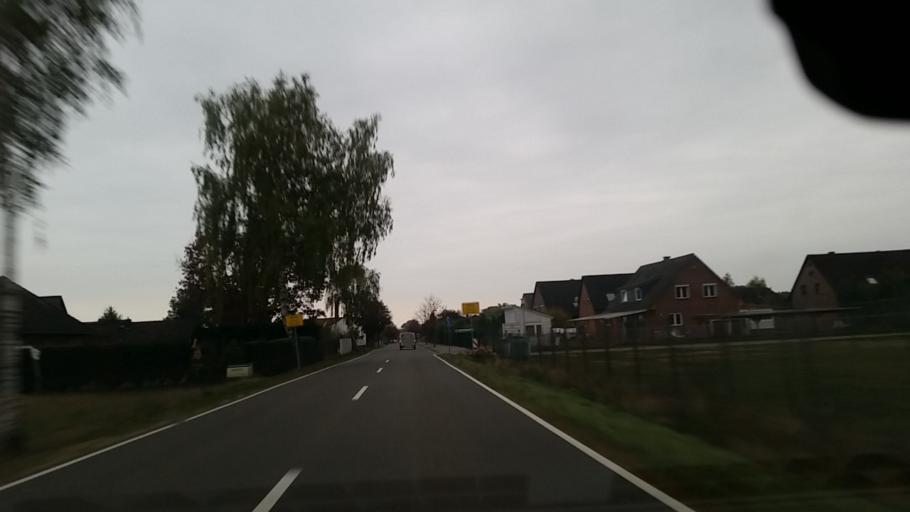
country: DE
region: Lower Saxony
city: Barwedel
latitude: 52.5742
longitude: 10.7873
